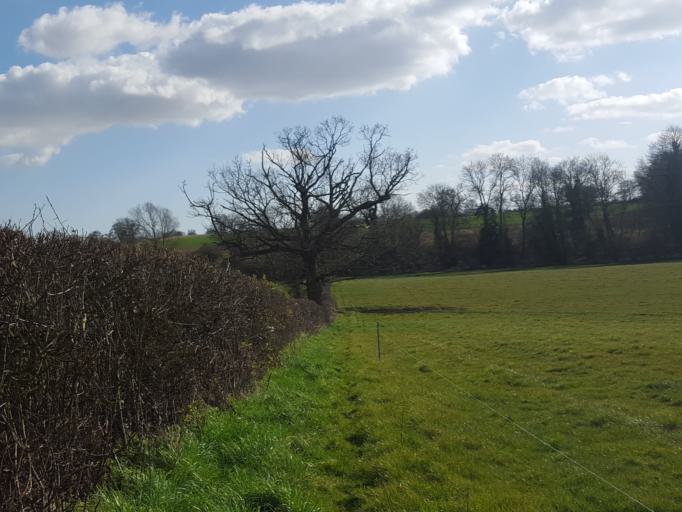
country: GB
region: England
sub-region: Essex
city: Little Clacton
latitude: 51.8698
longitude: 1.1148
